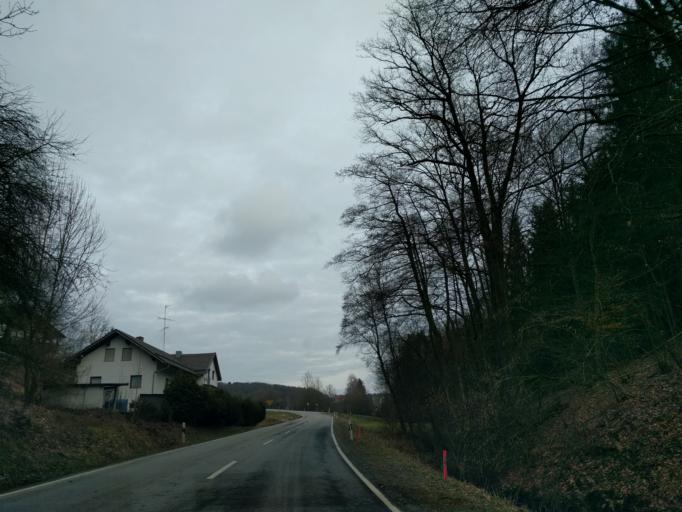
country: DE
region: Bavaria
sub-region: Lower Bavaria
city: Iggensbach
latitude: 48.7163
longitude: 13.1229
